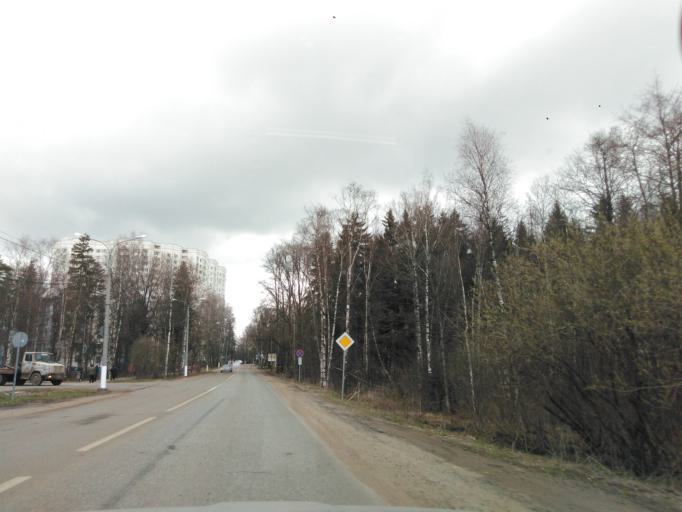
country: RU
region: Moskovskaya
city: Mendeleyevo
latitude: 56.0111
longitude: 37.2209
